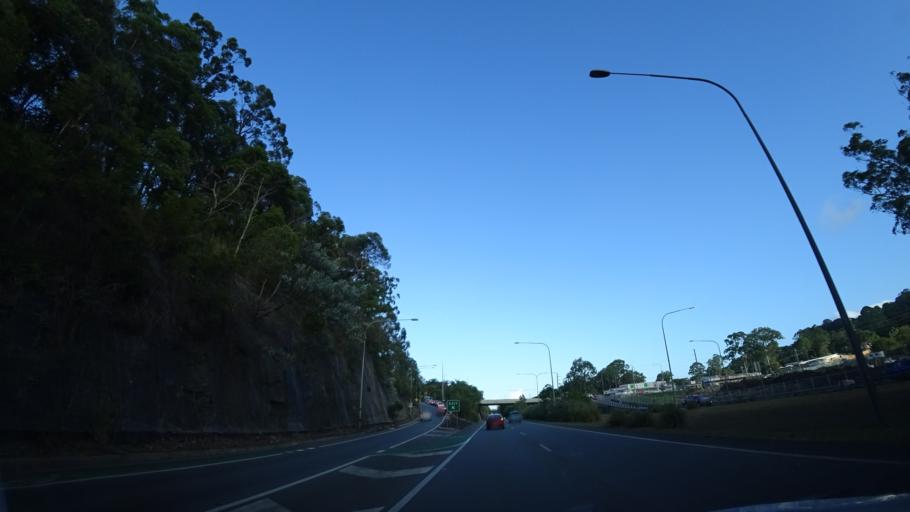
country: AU
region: Queensland
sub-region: Sunshine Coast
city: Buderim
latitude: -26.6618
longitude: 153.0496
